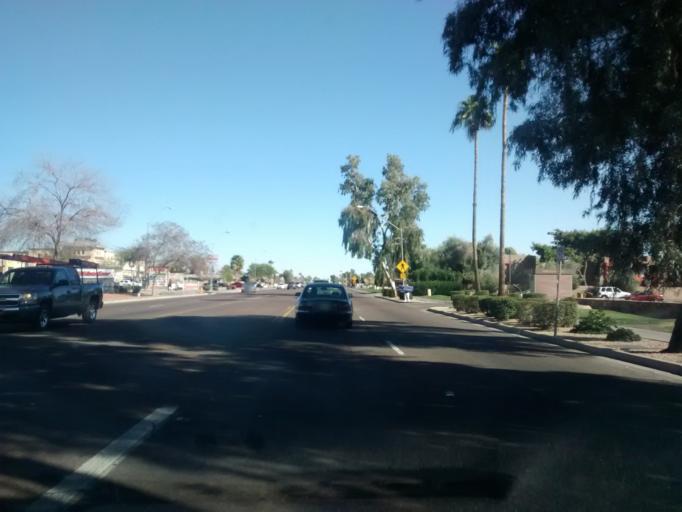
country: US
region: Arizona
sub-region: Maricopa County
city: Glendale
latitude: 33.5239
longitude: -112.2015
